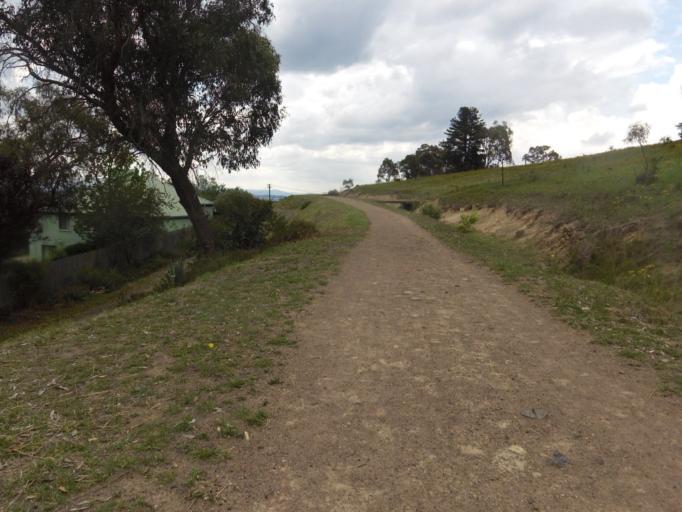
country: AU
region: Australian Capital Territory
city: Forrest
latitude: -35.3603
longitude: 149.1133
